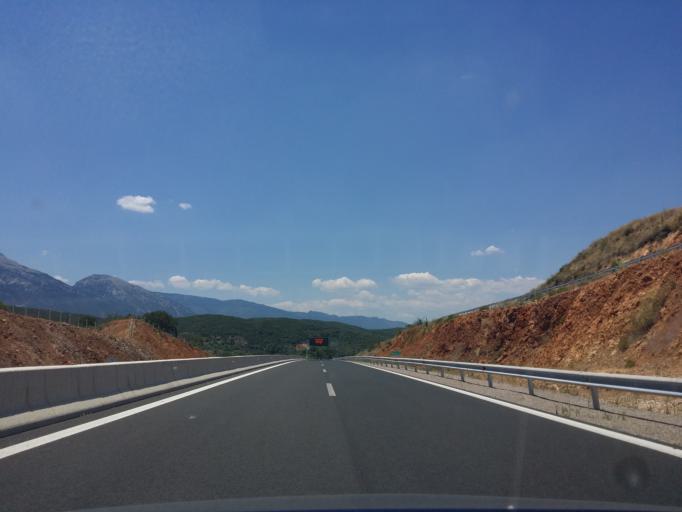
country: GR
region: Peloponnese
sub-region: Nomos Lakonias
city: Magoula
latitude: 37.1266
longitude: 22.4059
